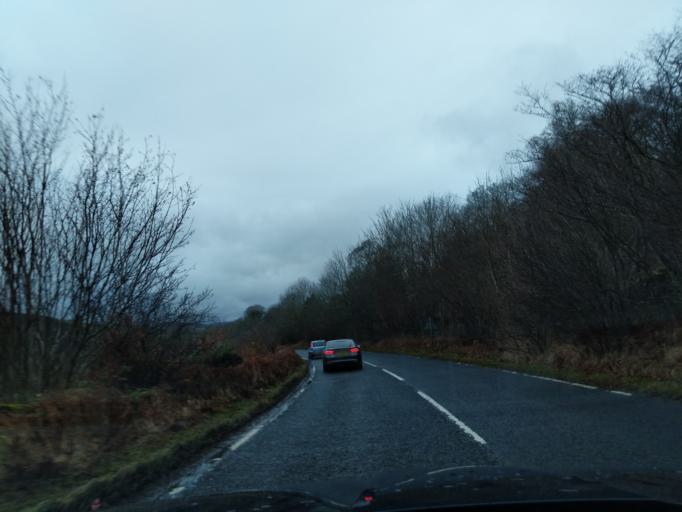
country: GB
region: Scotland
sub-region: The Scottish Borders
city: Galashiels
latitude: 55.6412
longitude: -2.8354
